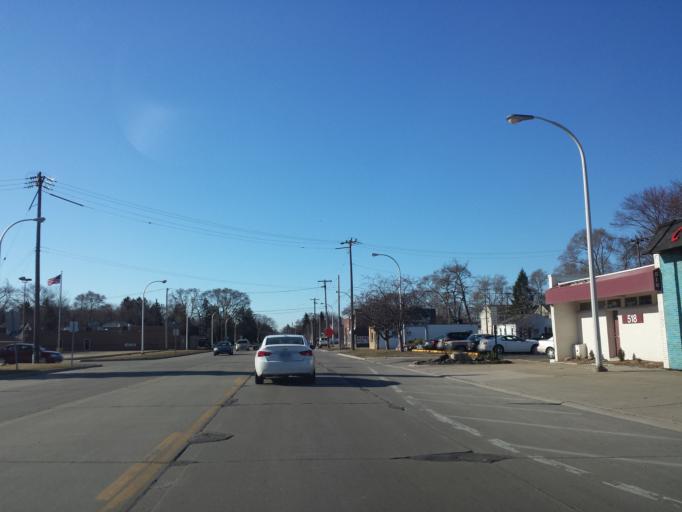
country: US
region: Michigan
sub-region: Oakland County
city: Clawson
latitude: 42.5295
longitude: -83.1461
